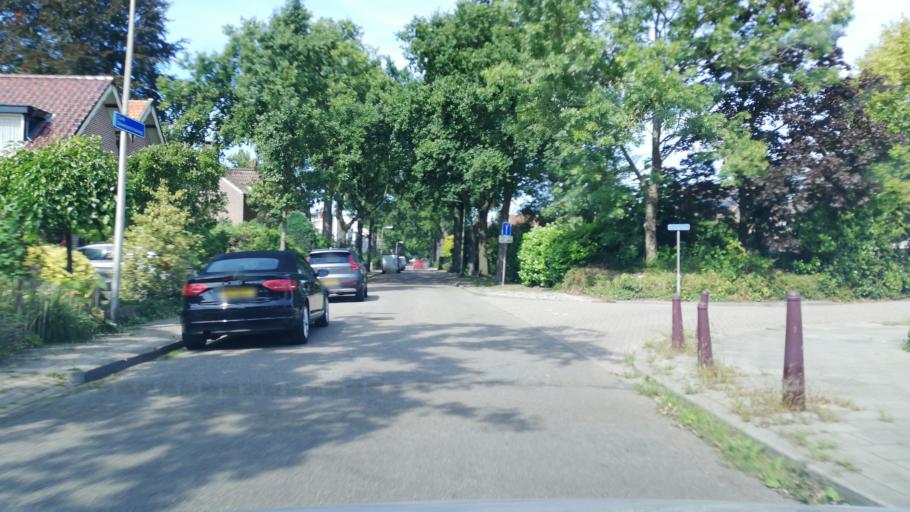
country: NL
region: Overijssel
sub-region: Gemeente Zwolle
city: Zwolle
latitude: 52.4941
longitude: 6.1043
